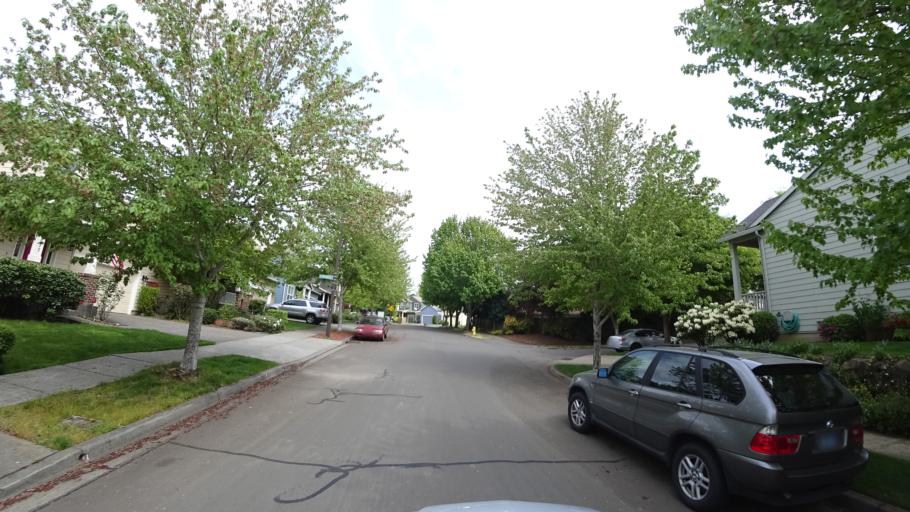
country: US
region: Oregon
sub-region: Washington County
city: Hillsboro
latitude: 45.5368
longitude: -122.9966
